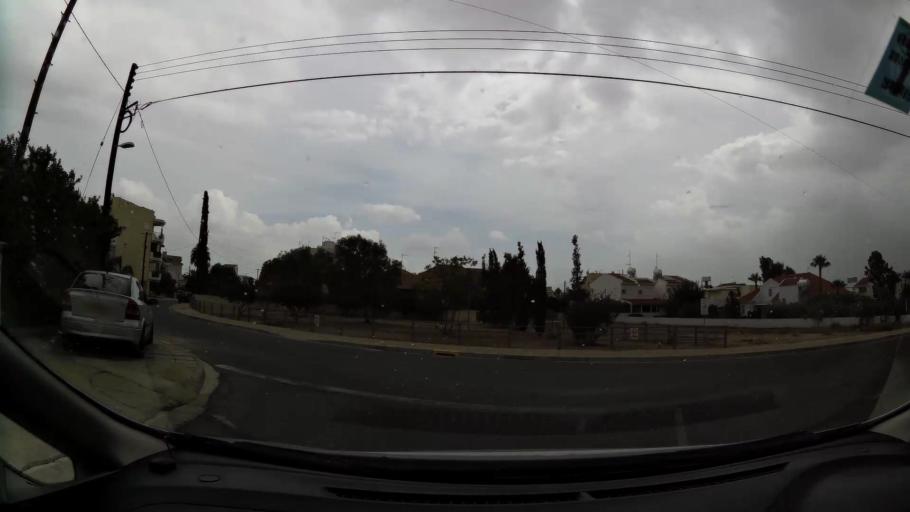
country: CY
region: Lefkosia
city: Geri
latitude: 35.1013
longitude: 33.3851
